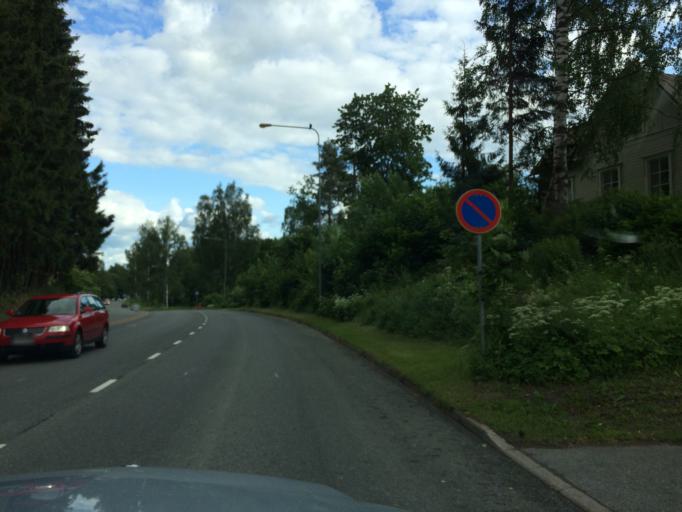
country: FI
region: Haeme
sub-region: Haemeenlinna
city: Haemeenlinna
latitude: 61.0105
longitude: 24.4470
